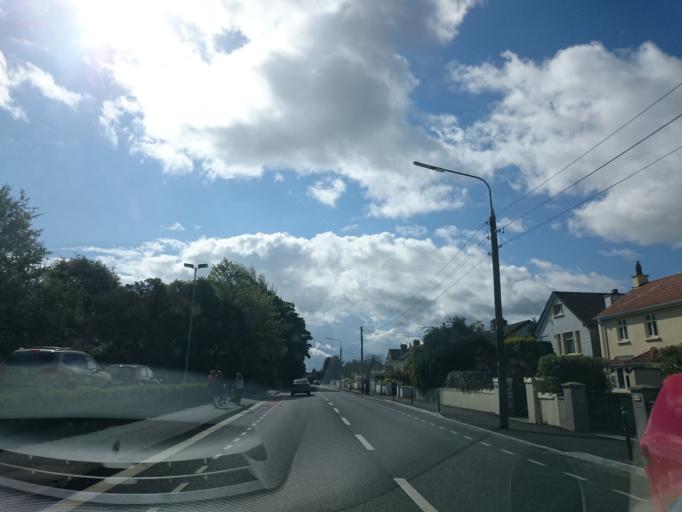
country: IE
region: Leinster
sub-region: Kilkenny
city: Kilkenny
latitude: 52.6639
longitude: -7.2511
